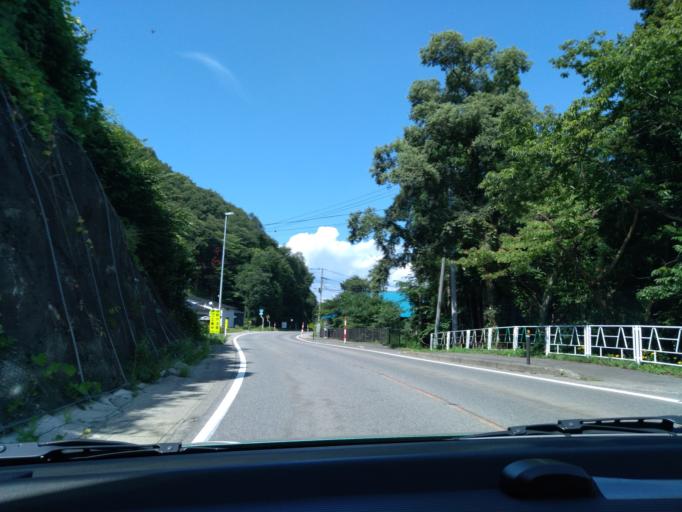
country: JP
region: Akita
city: Kakunodatemachi
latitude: 39.6828
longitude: 140.7069
